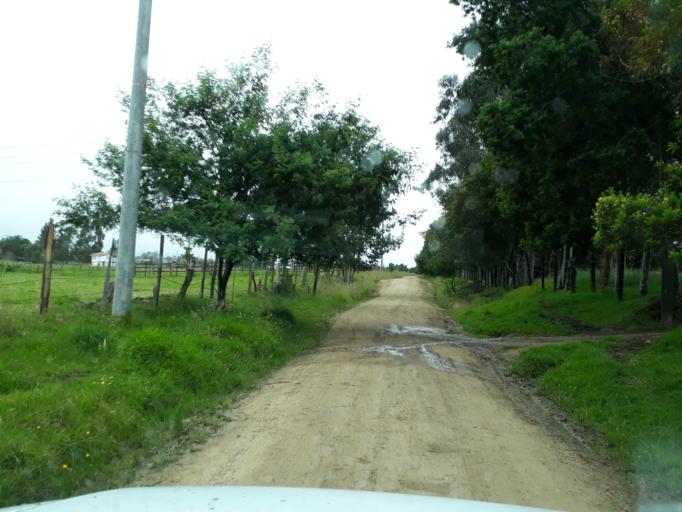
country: CO
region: Cundinamarca
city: Guasca
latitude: 4.8851
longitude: -73.8755
